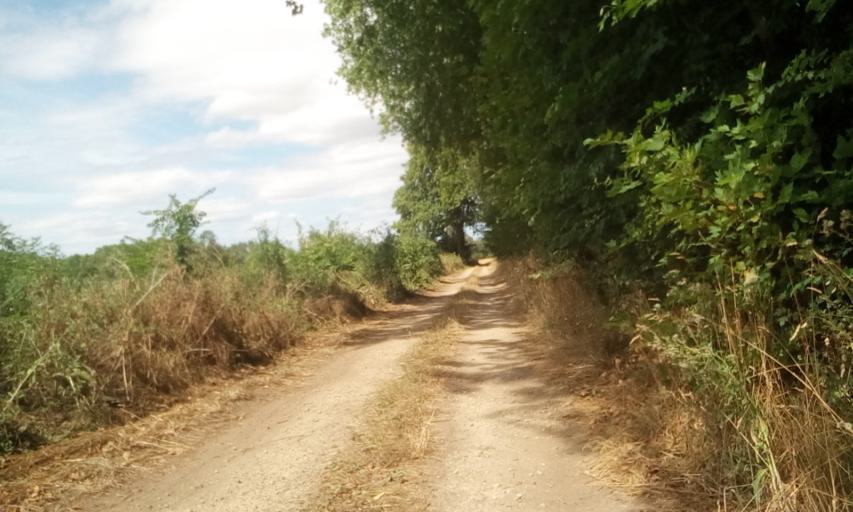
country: FR
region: Lower Normandy
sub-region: Departement du Calvados
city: Bellengreville
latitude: 49.1506
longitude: -0.2086
